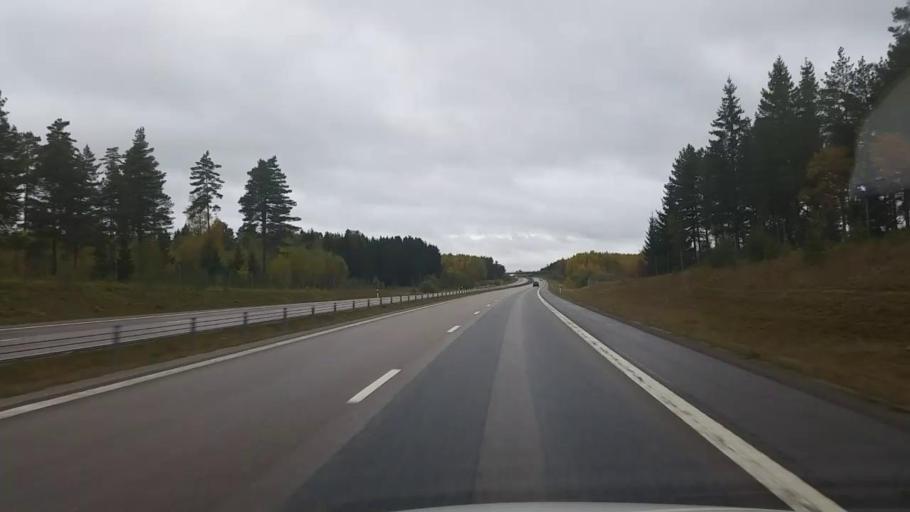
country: SE
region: Uppsala
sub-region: Osthammars Kommun
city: Bjorklinge
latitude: 60.1241
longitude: 17.5468
